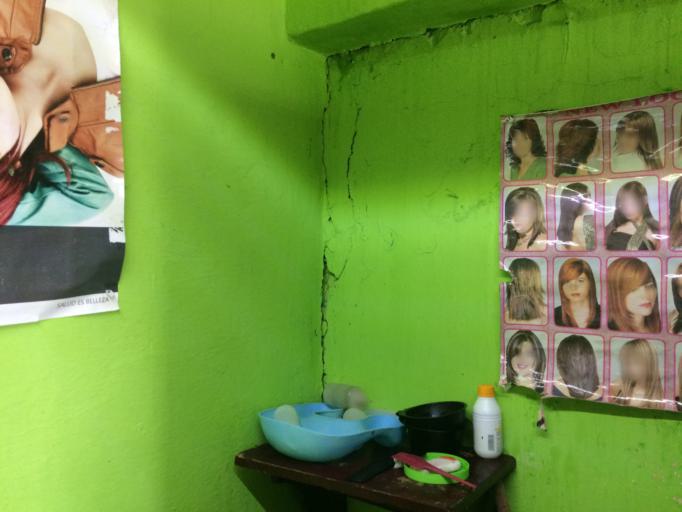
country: MX
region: Mexico
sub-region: Ocuilan
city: Plaza Nueva
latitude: 18.9159
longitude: -99.4534
